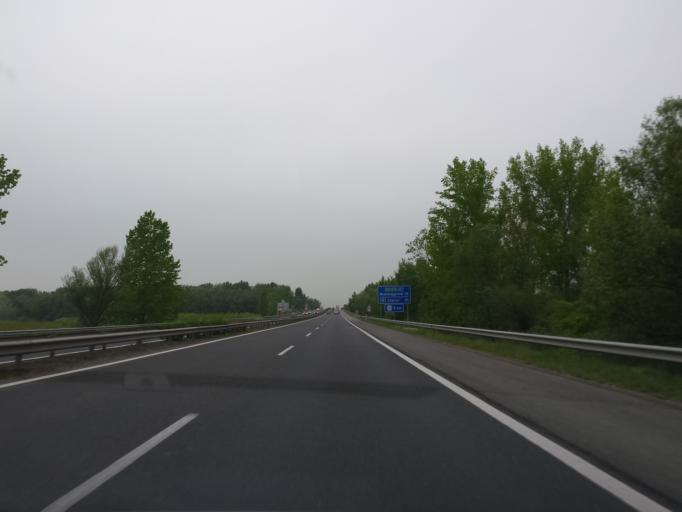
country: HU
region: Gyor-Moson-Sopron
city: Gyor
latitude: 47.6512
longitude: 17.6086
